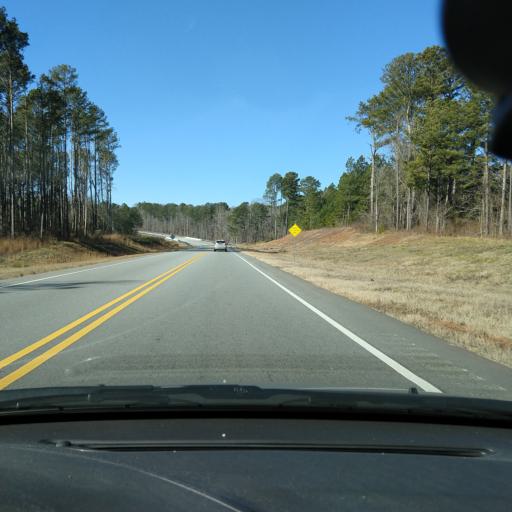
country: US
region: Georgia
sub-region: Walton County
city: Social Circle
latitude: 33.6408
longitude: -83.7044
